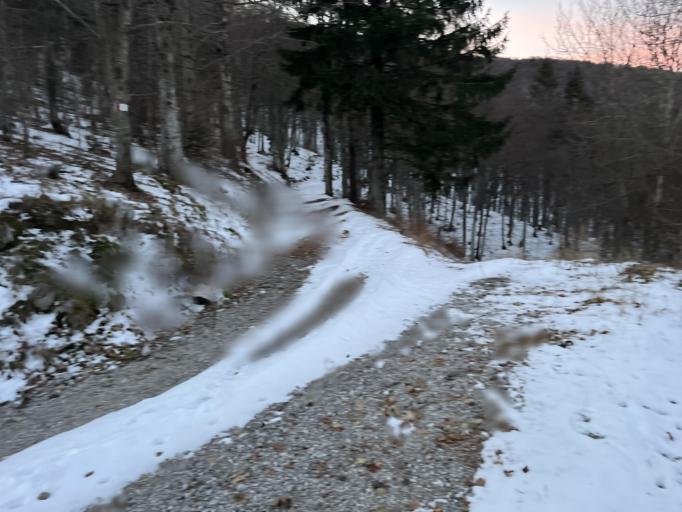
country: IT
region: Friuli Venezia Giulia
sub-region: Provincia di Udine
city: Forgaria nel Friuli
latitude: 46.2771
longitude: 13.0082
